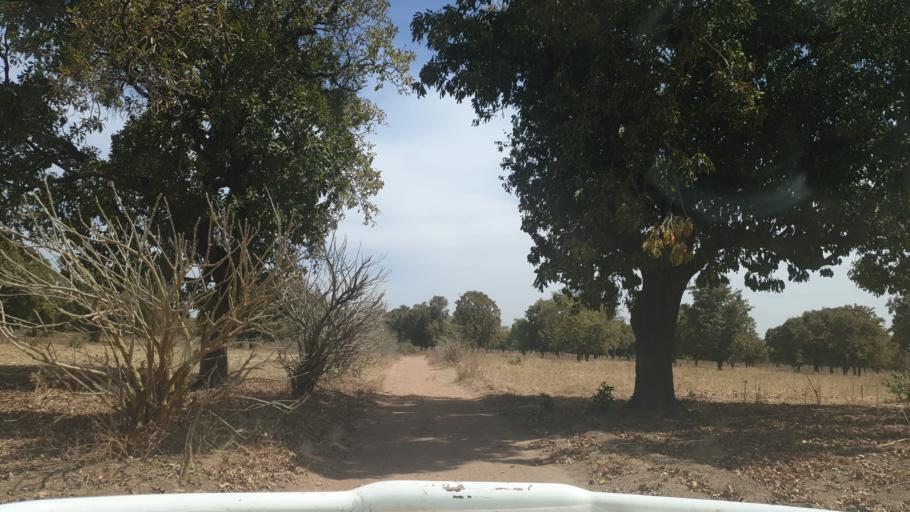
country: ML
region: Sikasso
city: Yorosso
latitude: 12.2912
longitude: -4.6677
